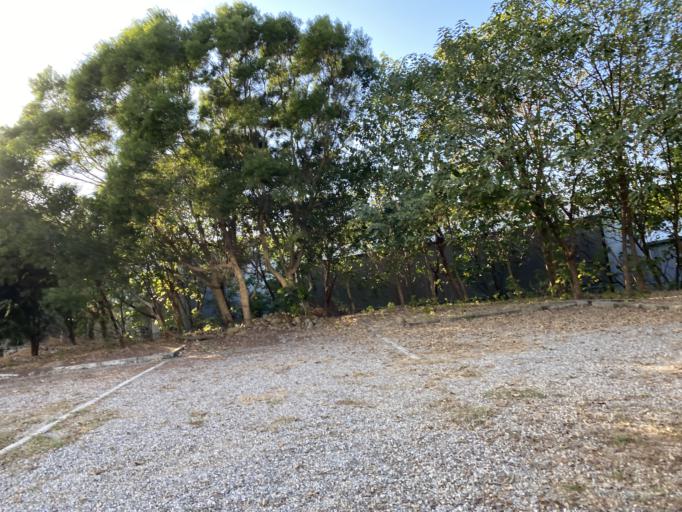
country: TW
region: Taiwan
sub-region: Changhua
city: Chang-hua
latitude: 24.1354
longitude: 120.5999
